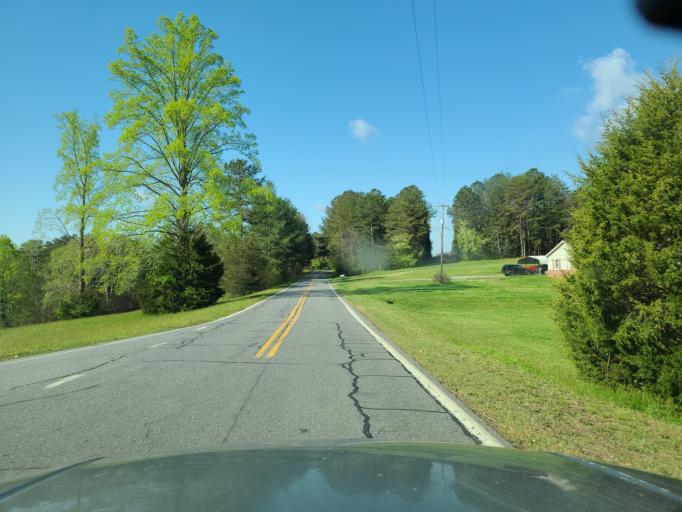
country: US
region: North Carolina
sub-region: Rutherford County
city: Forest City
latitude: 35.4102
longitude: -81.8600
